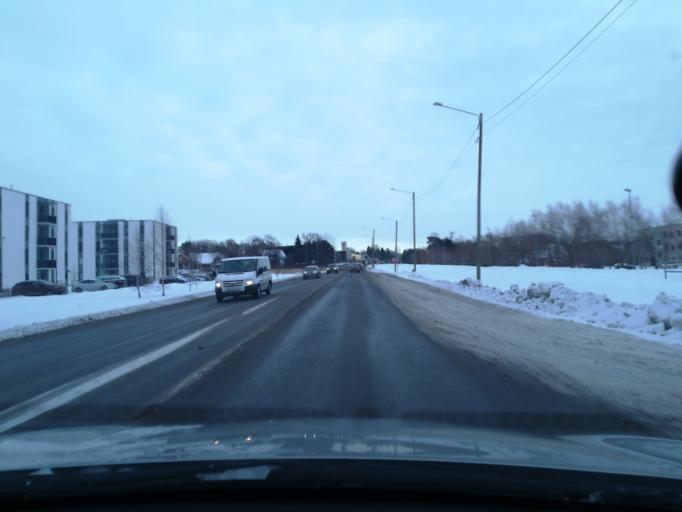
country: EE
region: Harju
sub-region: Saue vald
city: Laagri
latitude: 59.4290
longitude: 24.6195
